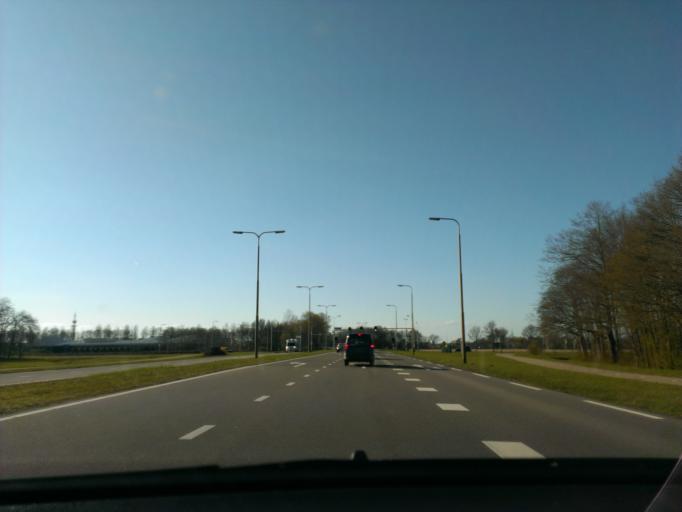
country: NL
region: Overijssel
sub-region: Gemeente Zwolle
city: Zwolle
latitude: 52.5288
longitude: 6.1569
